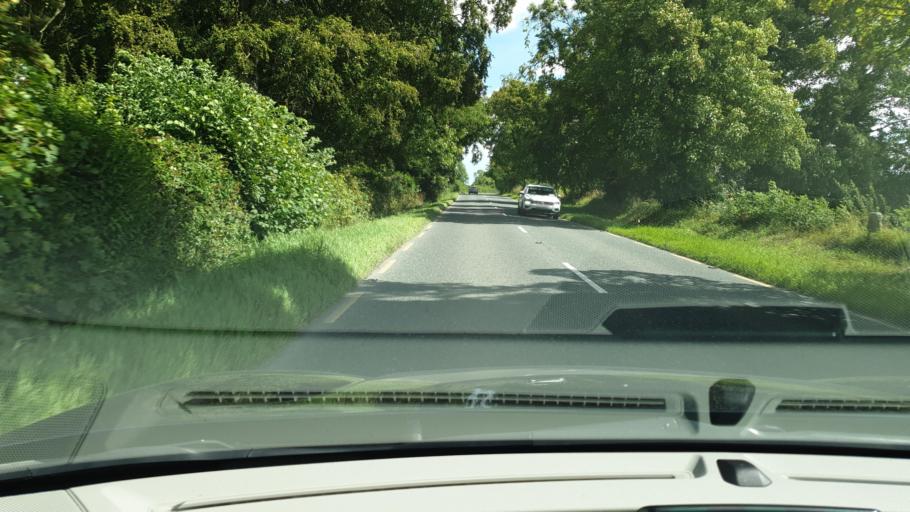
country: IE
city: Confey
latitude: 53.4364
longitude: -6.5242
